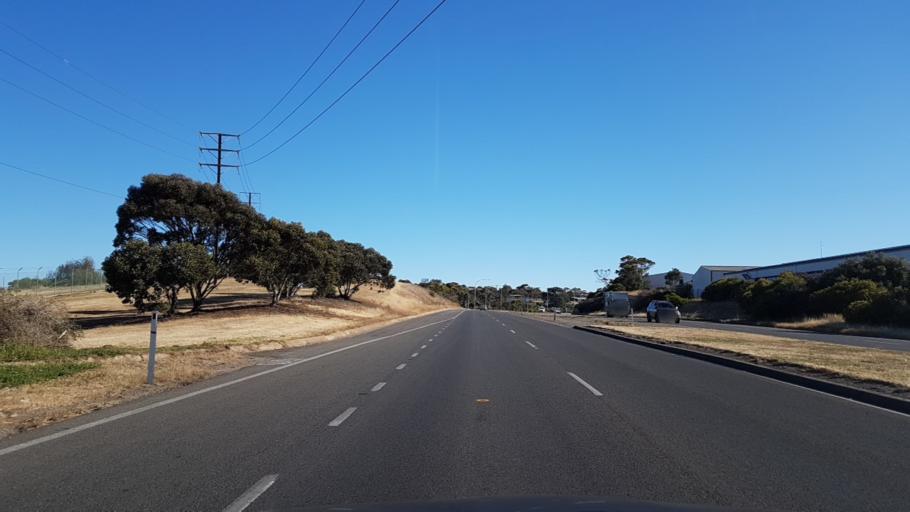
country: AU
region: South Australia
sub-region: Onkaparinga
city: Morphett Vale
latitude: -35.1161
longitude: 138.4909
